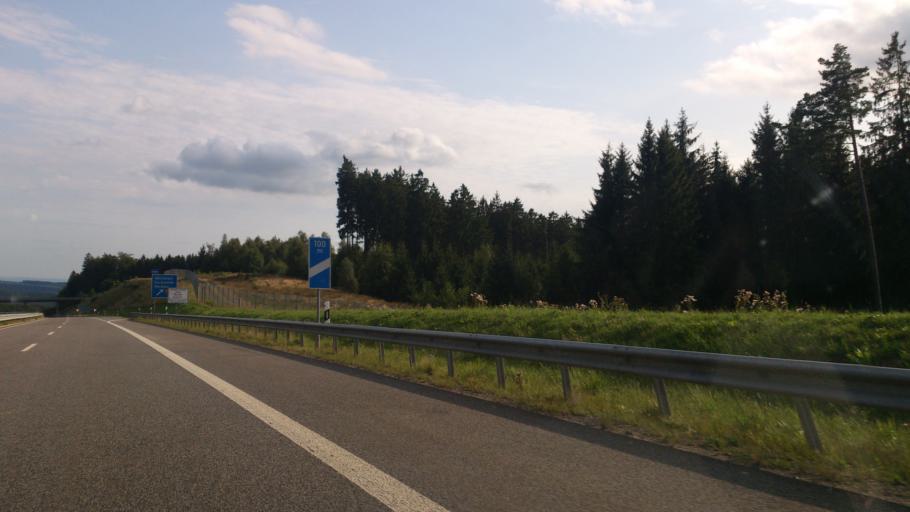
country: DE
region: Rheinland-Pfalz
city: Kradenbach
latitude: 50.2552
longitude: 6.8257
